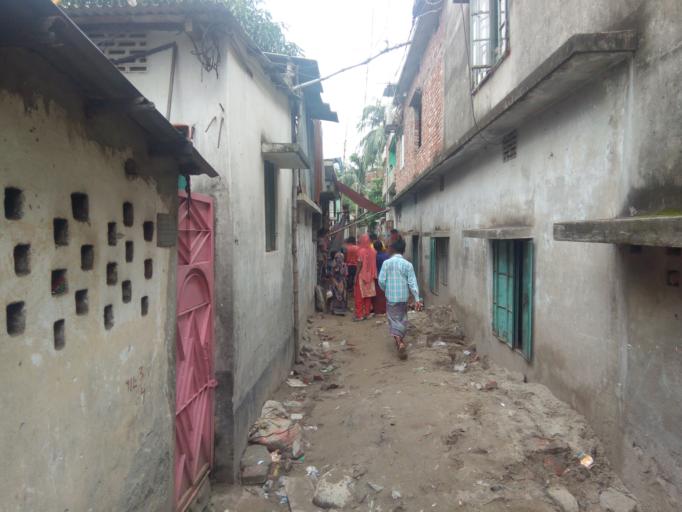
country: BD
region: Dhaka
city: Azimpur
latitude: 23.7167
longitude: 90.3753
